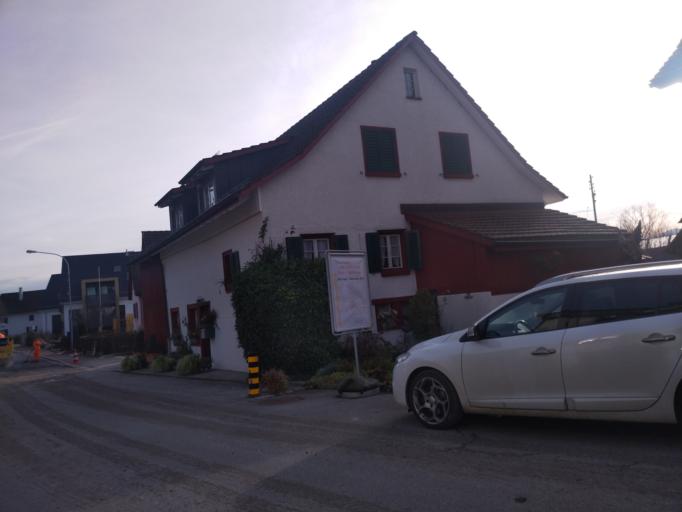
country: CH
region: Zurich
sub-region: Bezirk Dietikon
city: Unterengstringen
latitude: 47.4113
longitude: 8.4441
